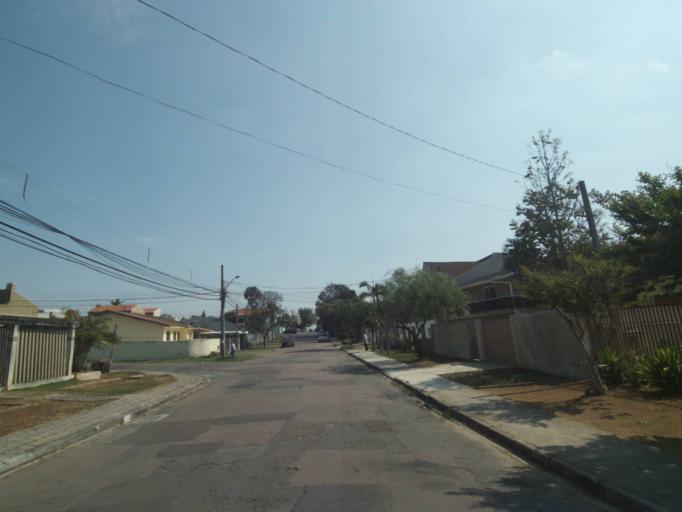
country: BR
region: Parana
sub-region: Curitiba
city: Curitiba
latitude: -25.4808
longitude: -49.3264
